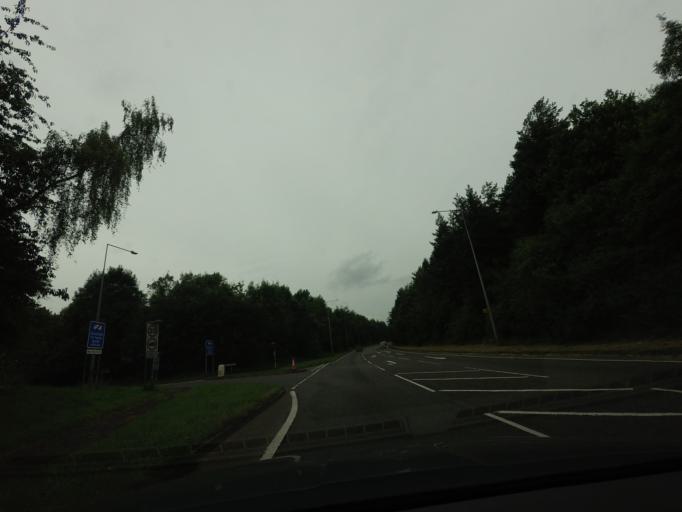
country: GB
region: England
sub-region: Telford and Wrekin
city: Ironbridge
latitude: 52.6433
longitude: -2.4815
